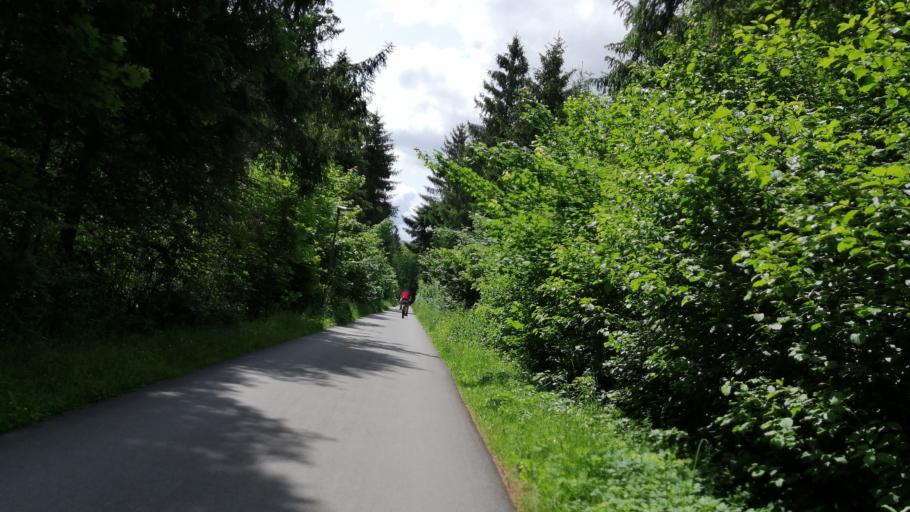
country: DE
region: Bavaria
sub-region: Upper Bavaria
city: Unterhaching
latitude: 48.0852
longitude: 11.6064
